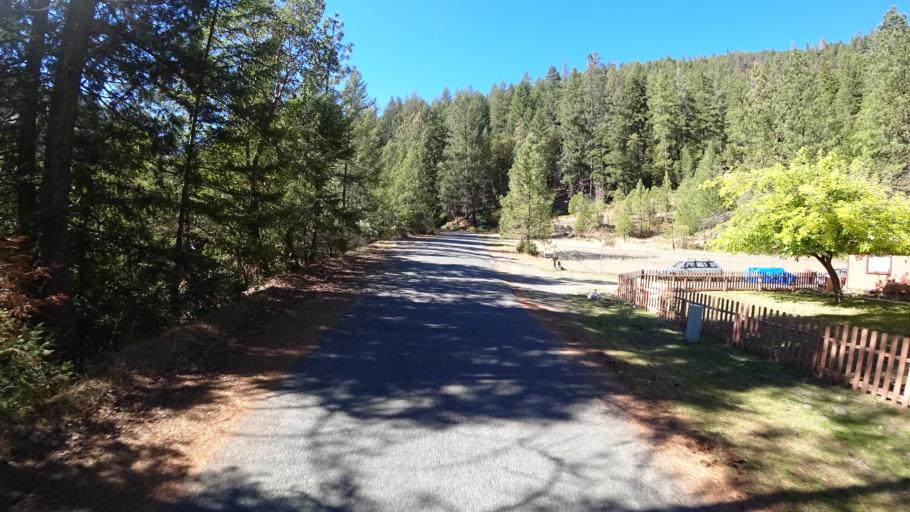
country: US
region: California
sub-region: Siskiyou County
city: Happy Camp
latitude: 41.3012
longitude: -123.1390
